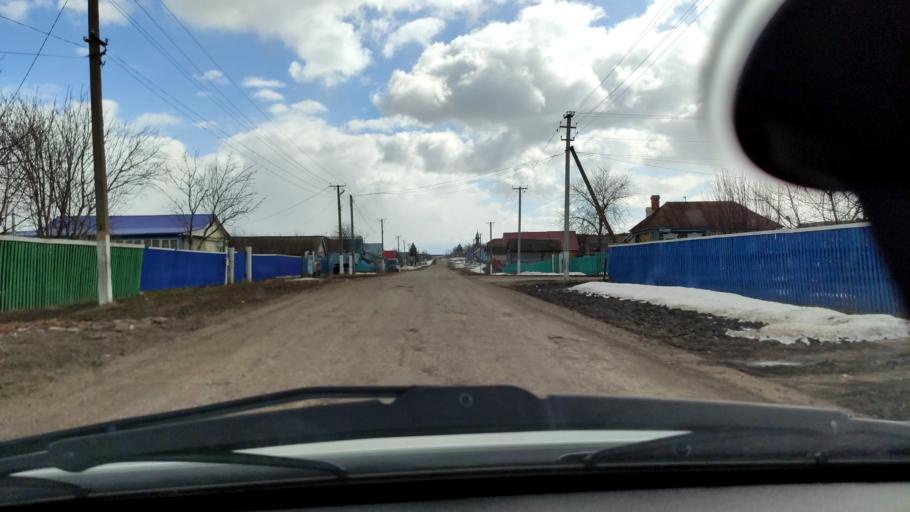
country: RU
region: Bashkortostan
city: Tolbazy
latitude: 54.1723
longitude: 55.9532
